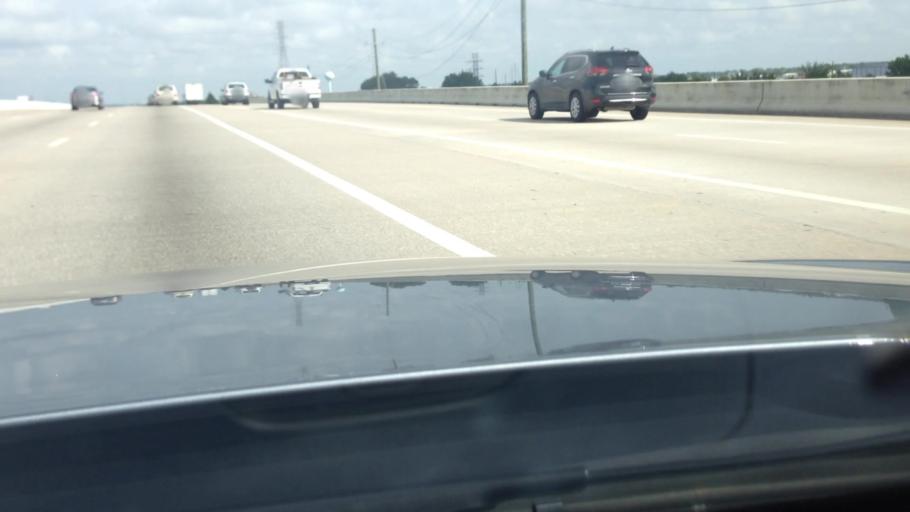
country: US
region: Texas
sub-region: Harris County
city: Hudson
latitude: 29.9442
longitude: -95.5254
